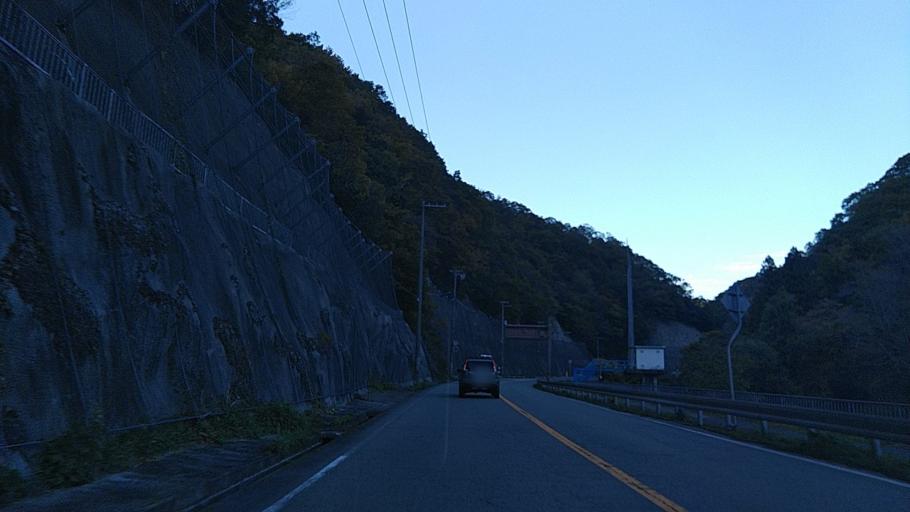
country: JP
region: Osaka
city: Ikeda
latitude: 34.9366
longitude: 135.4088
